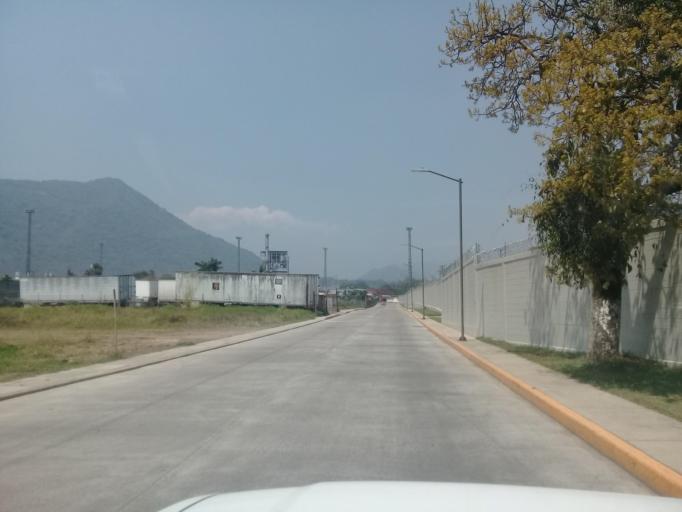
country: MX
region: Veracruz
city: Ixtac Zoquitlan
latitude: 18.8622
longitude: -97.0612
